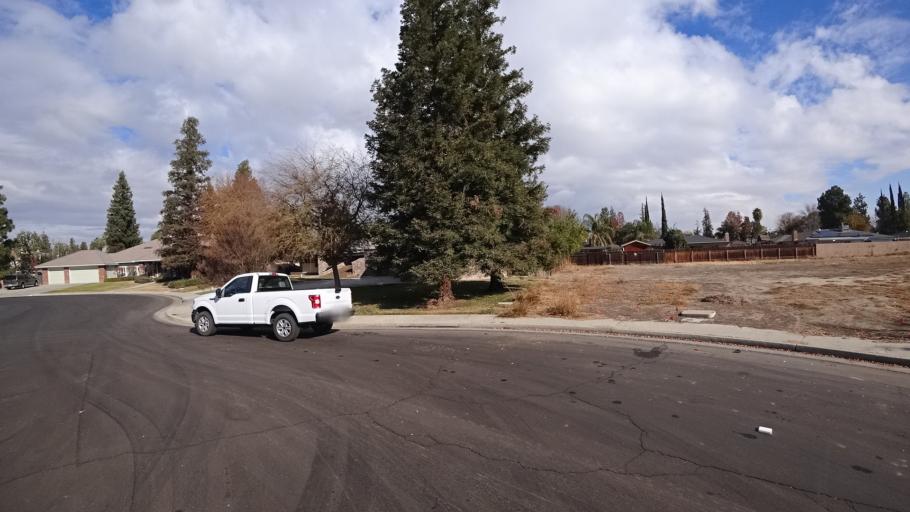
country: US
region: California
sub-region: Kern County
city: Greenacres
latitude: 35.3400
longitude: -119.0847
